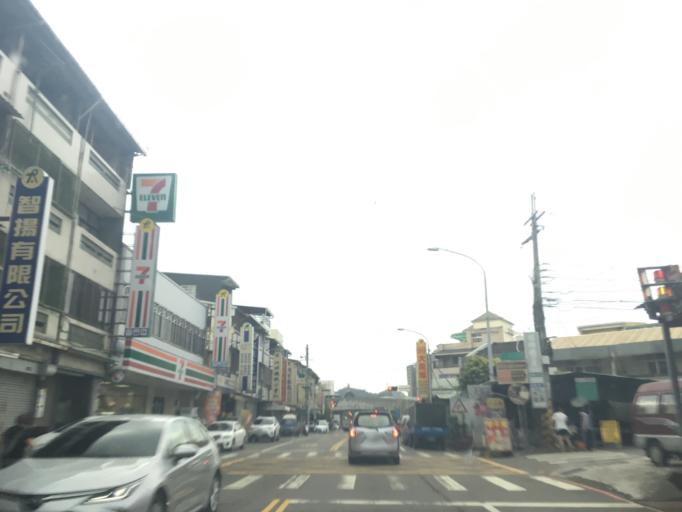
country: TW
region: Taiwan
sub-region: Taichung City
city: Taichung
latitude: 24.1547
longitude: 120.7335
